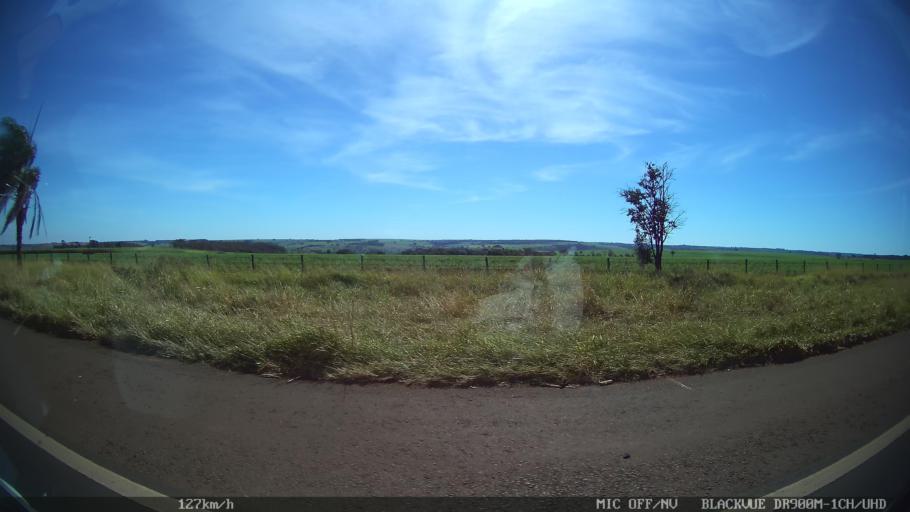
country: BR
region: Sao Paulo
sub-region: Franca
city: Franca
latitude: -20.5599
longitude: -47.6071
